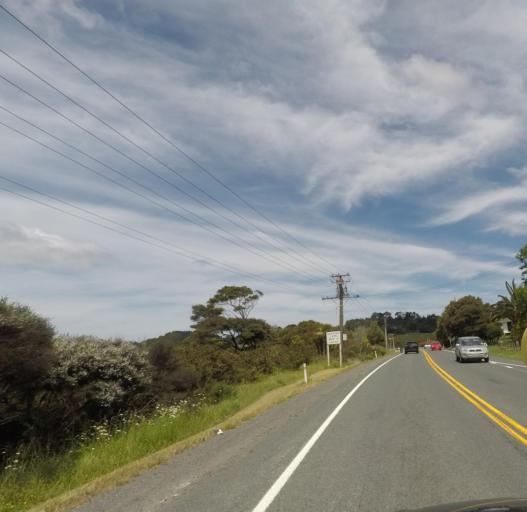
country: NZ
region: Auckland
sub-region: Auckland
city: Rothesay Bay
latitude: -36.6832
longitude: 174.7003
